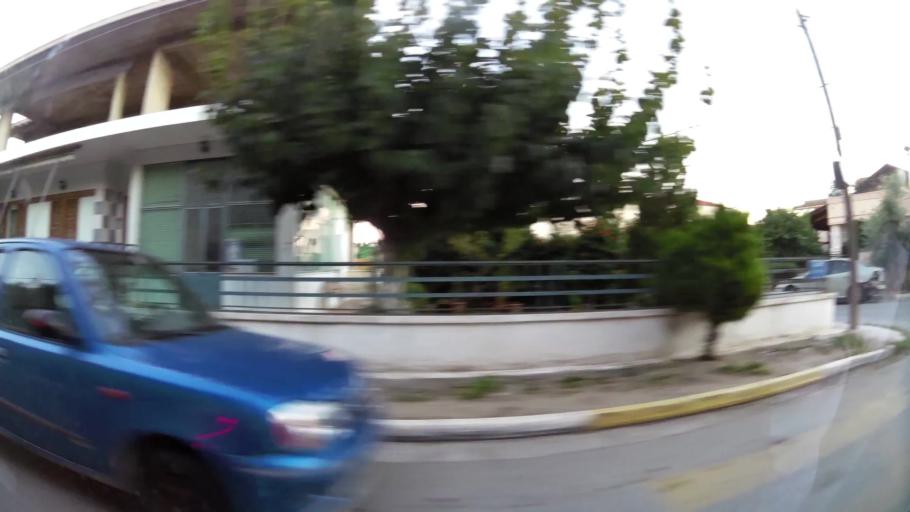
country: GR
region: Attica
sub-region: Nomarchia Anatolikis Attikis
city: Paiania
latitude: 37.9497
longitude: 23.8565
